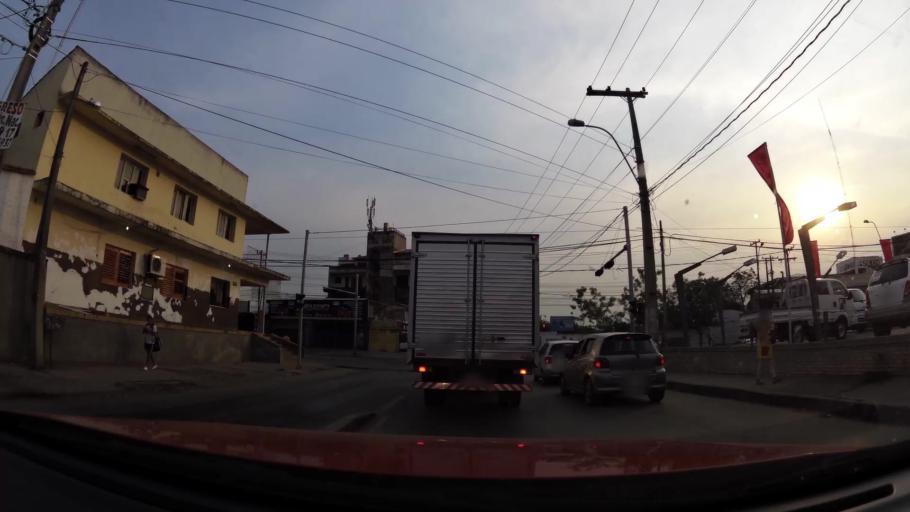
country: PY
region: Central
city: Lambare
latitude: -25.3340
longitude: -57.5898
